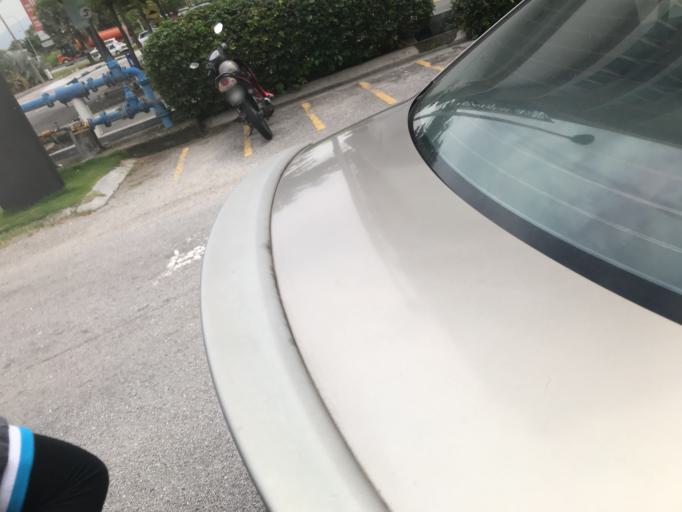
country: MY
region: Perak
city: Ipoh
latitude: 4.6215
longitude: 101.1166
